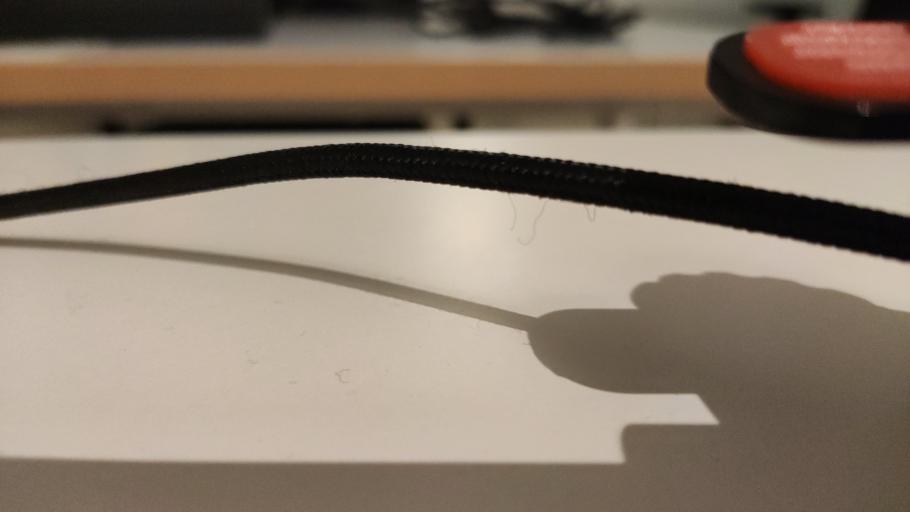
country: RU
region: Moskovskaya
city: Rogachevo
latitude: 56.4311
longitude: 37.1808
